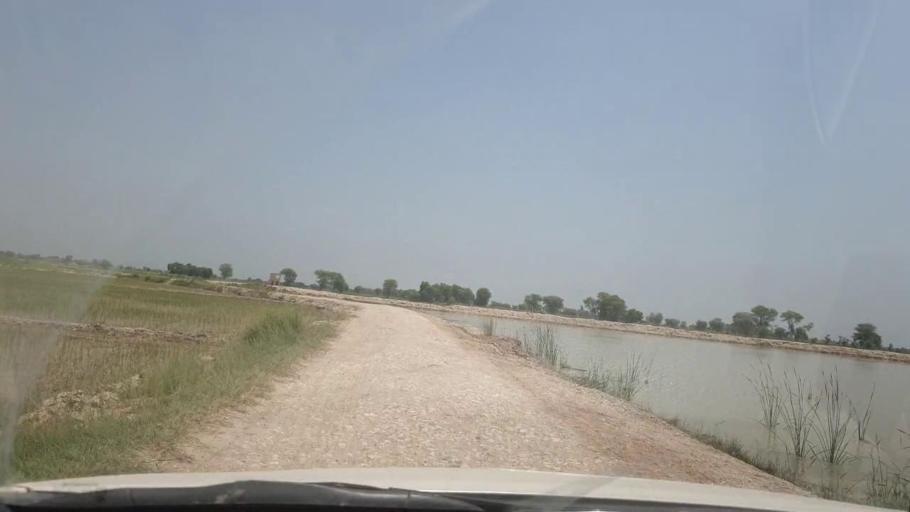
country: PK
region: Sindh
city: Lakhi
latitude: 27.8651
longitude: 68.7185
